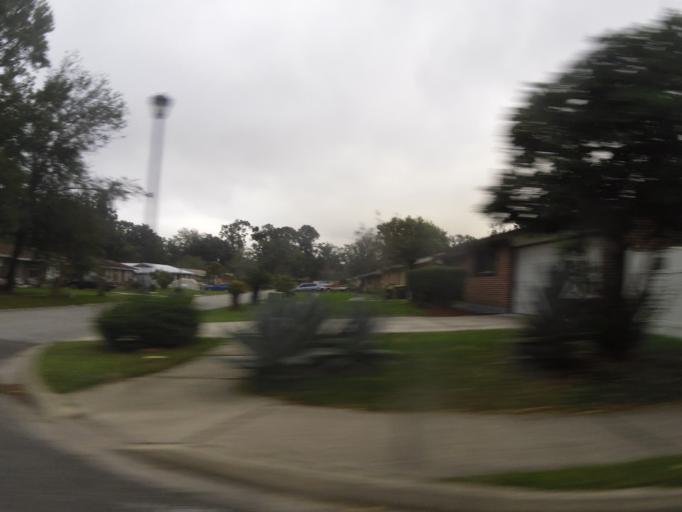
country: US
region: Florida
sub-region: Clay County
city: Bellair-Meadowbrook Terrace
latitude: 30.2754
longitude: -81.7476
